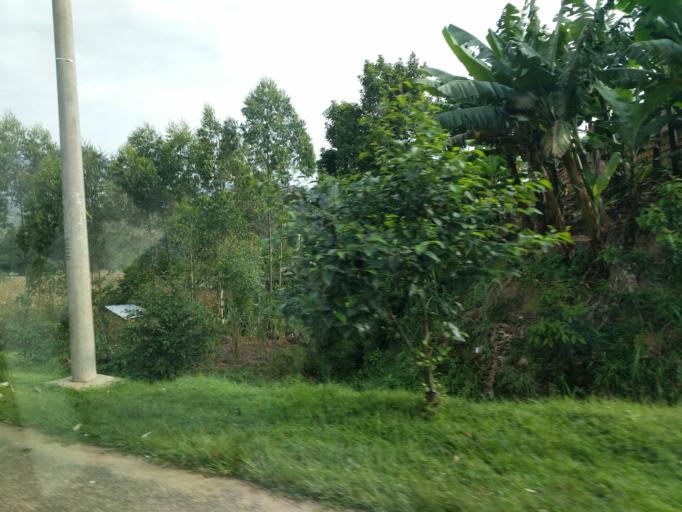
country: RW
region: Northern Province
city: Musanze
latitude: -1.6571
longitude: 29.8253
